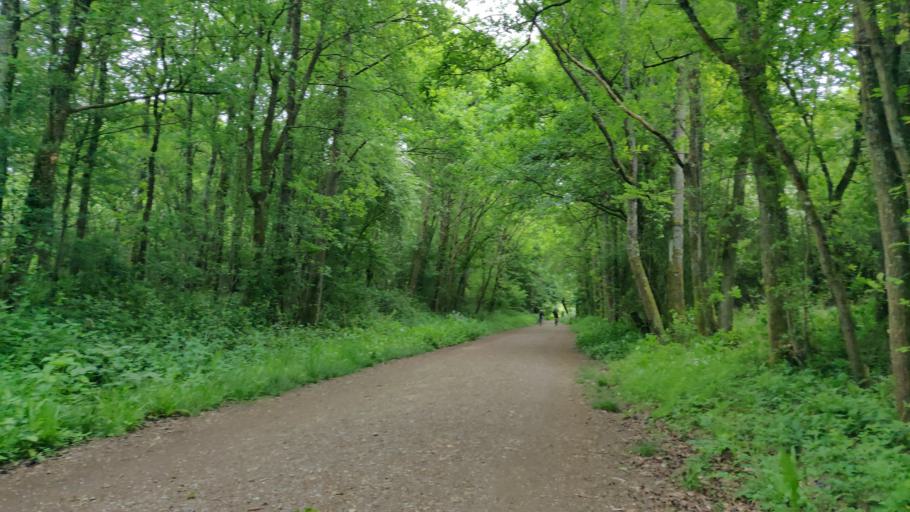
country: GB
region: England
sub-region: West Sussex
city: Southwater
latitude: 51.0128
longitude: -0.3343
